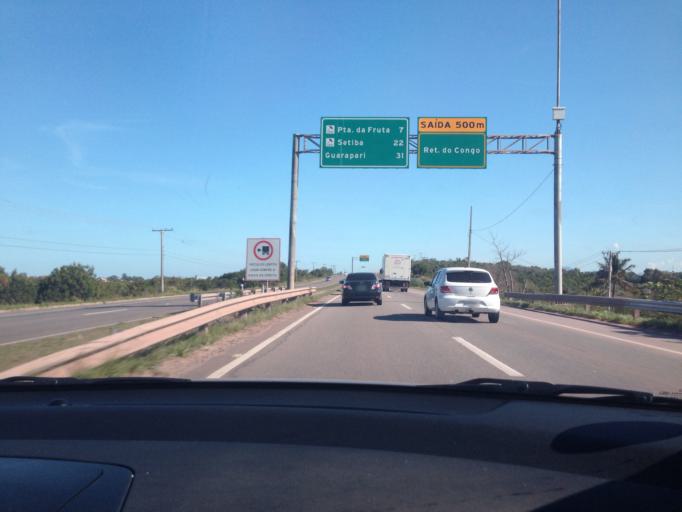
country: BR
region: Espirito Santo
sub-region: Vila Velha
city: Vila Velha
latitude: -20.4611
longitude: -40.3443
